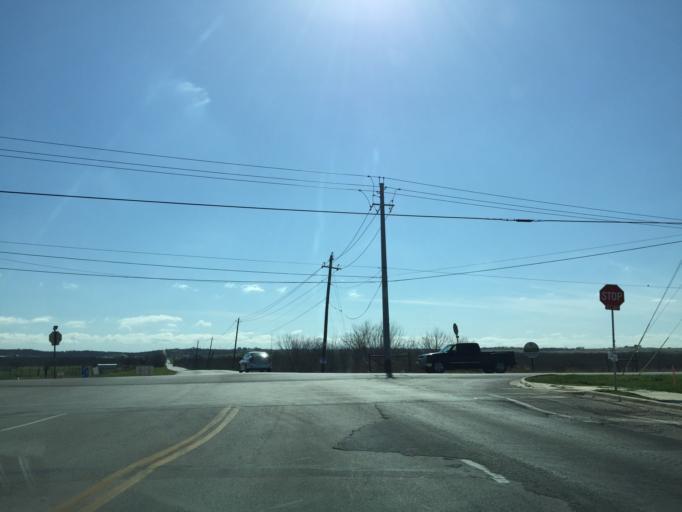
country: US
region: Texas
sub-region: Travis County
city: Garfield
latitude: 30.1542
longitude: -97.6400
